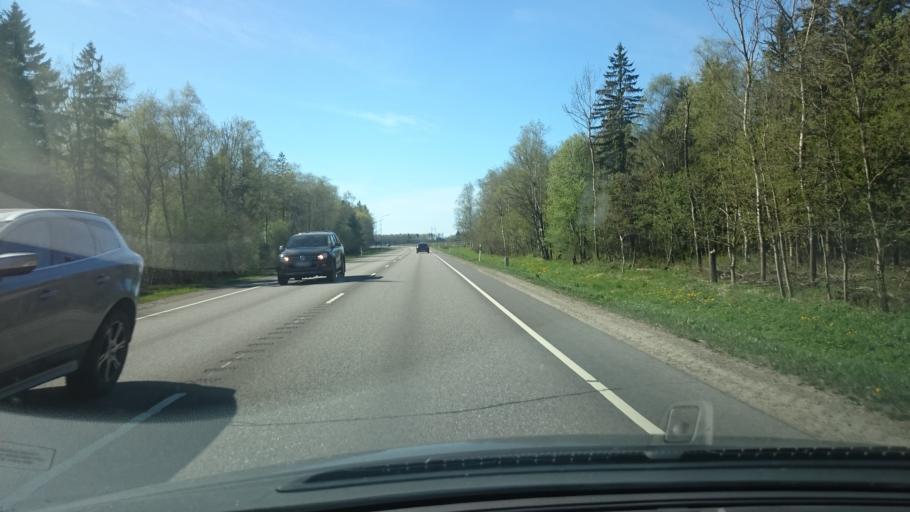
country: EE
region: Ida-Virumaa
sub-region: Kohtla-Jaerve linn
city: Kohtla-Jarve
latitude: 59.4173
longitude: 27.2896
